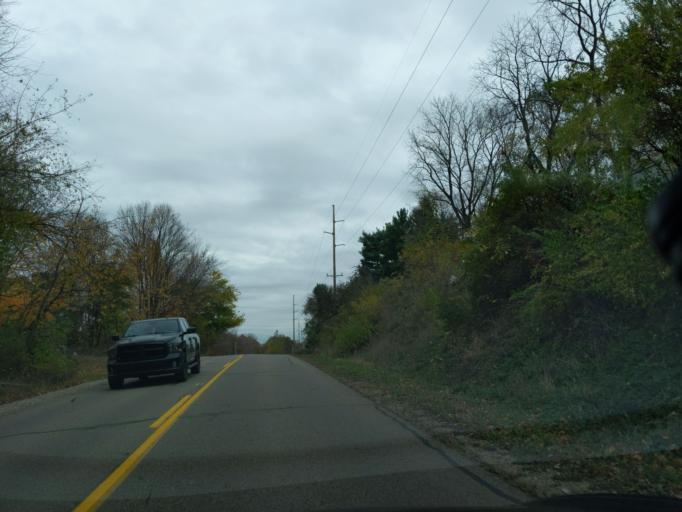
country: US
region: Michigan
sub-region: Eaton County
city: Eaton Rapids
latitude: 42.5239
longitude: -84.6233
